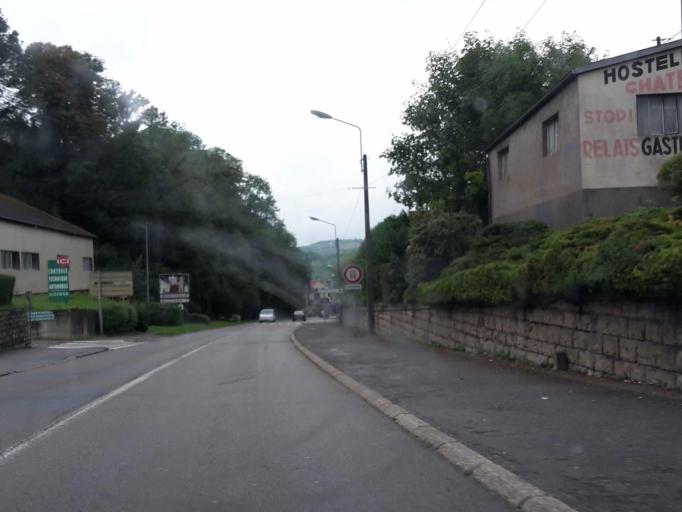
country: FR
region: Franche-Comte
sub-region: Departement du Doubs
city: Baume-les-Dames
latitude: 47.3508
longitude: 6.3662
